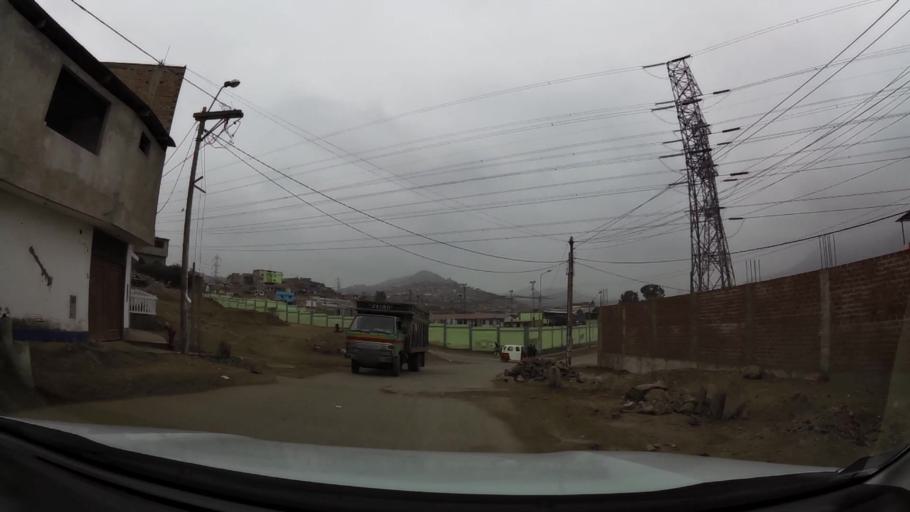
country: PE
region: Lima
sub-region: Lima
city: Cieneguilla
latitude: -12.2298
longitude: -76.9081
